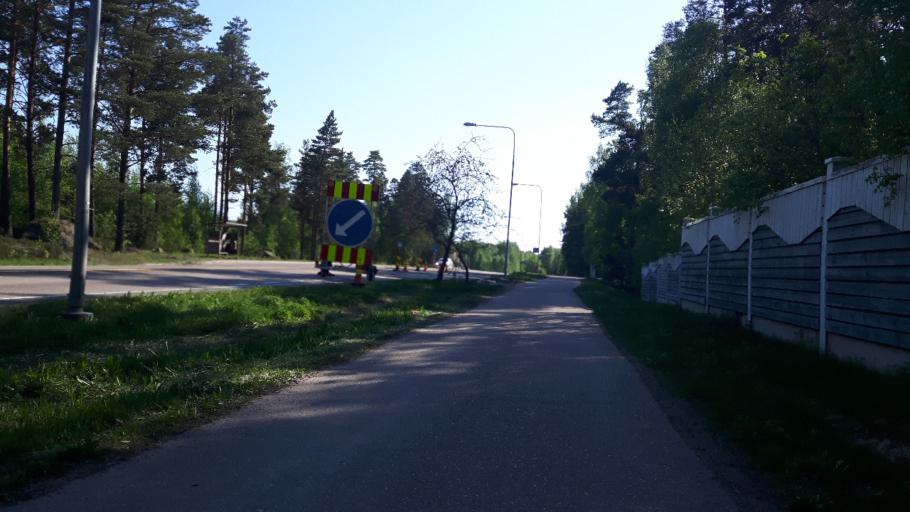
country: FI
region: Kymenlaakso
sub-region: Kotka-Hamina
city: Kotka
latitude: 60.4417
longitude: 26.8864
